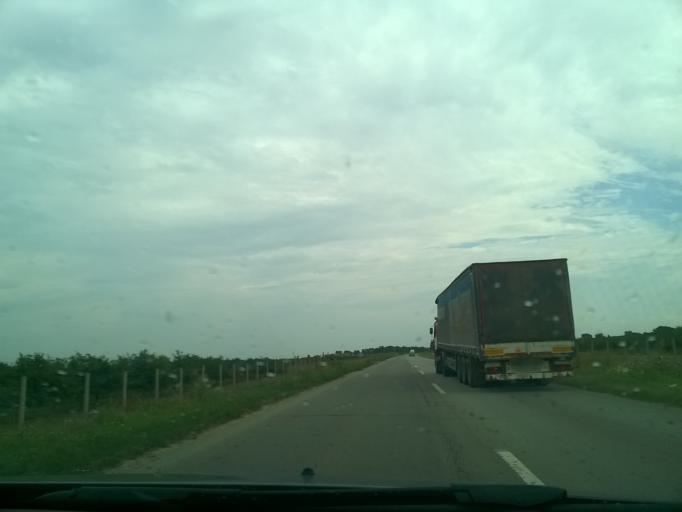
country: RS
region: Autonomna Pokrajina Vojvodina
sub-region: Srednjebanatski Okrug
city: Zrenjanin
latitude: 45.4018
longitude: 20.3802
